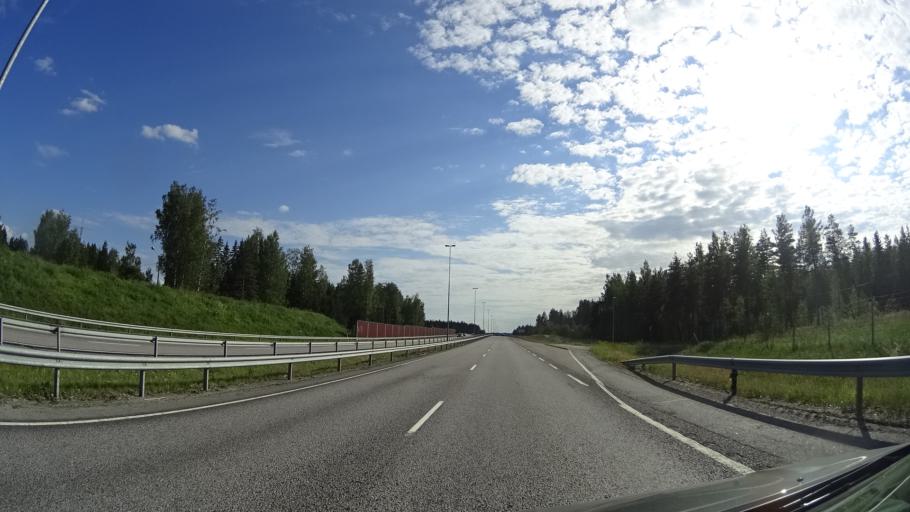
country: FI
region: South Karelia
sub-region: Lappeenranta
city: Joutseno
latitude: 61.0930
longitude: 28.3663
